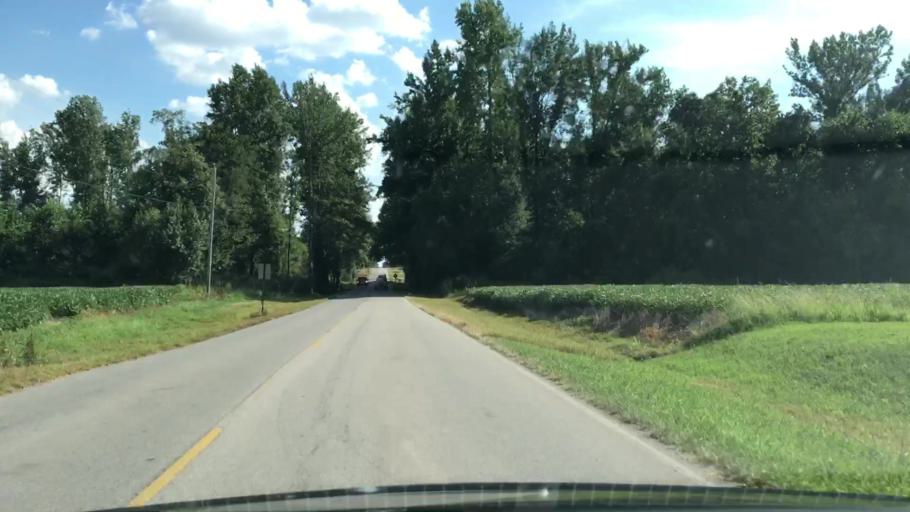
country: US
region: Alabama
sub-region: Madison County
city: Harvest
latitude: 34.8857
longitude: -86.7487
